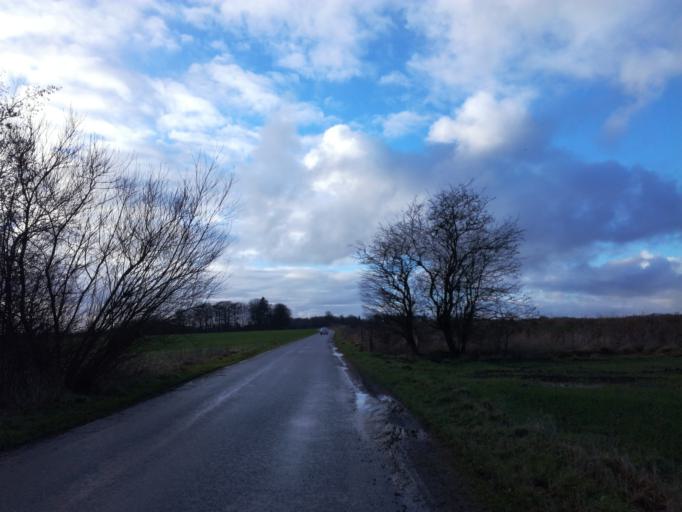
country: DK
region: South Denmark
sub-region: Fredericia Kommune
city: Taulov
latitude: 55.5629
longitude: 9.6508
